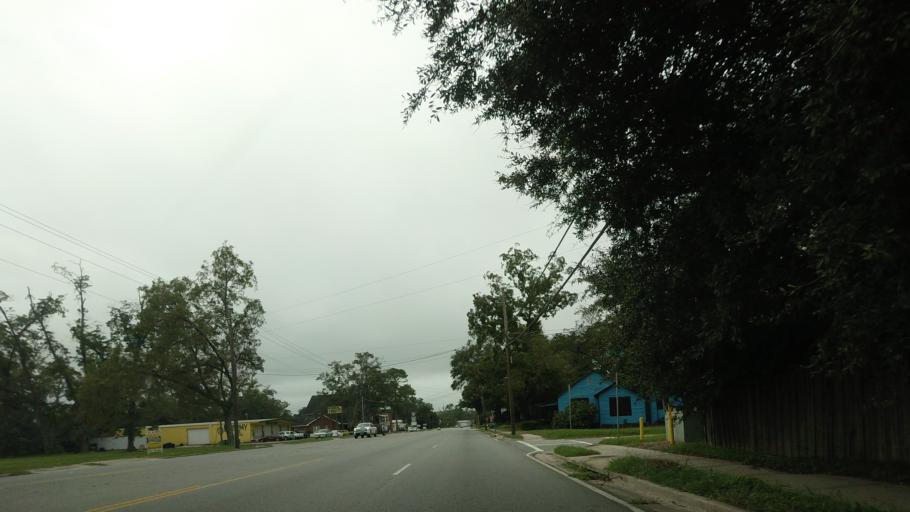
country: US
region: Georgia
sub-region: Lowndes County
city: Valdosta
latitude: 30.8247
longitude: -83.2946
